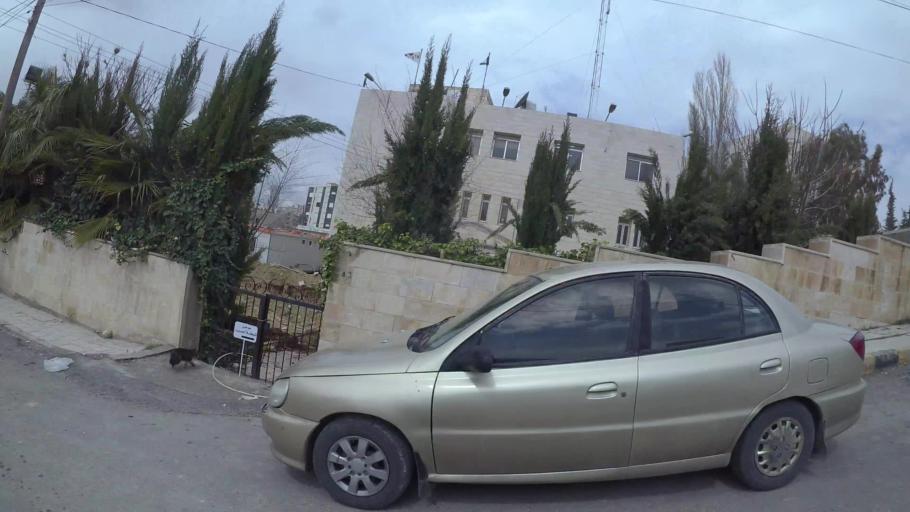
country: JO
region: Amman
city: Umm as Summaq
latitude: 31.9025
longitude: 35.8397
